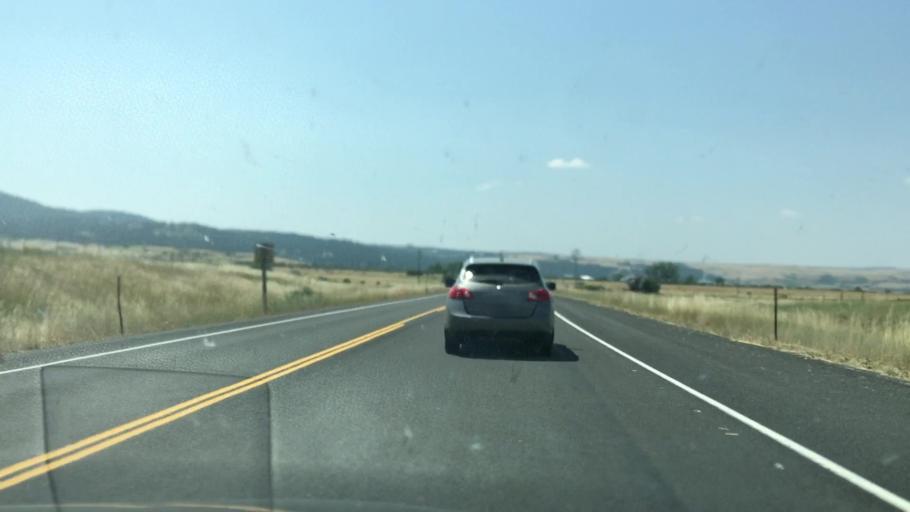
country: US
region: Idaho
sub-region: Idaho County
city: Grangeville
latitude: 45.9052
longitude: -116.1739
